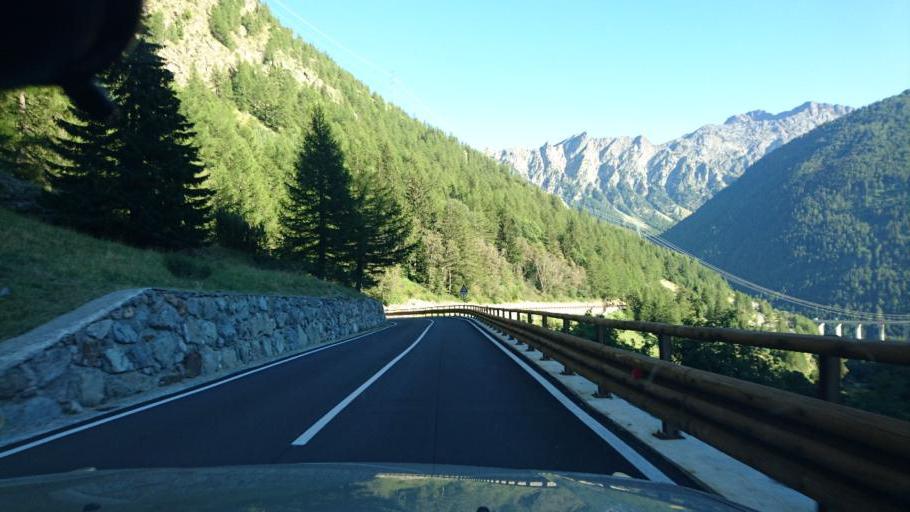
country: IT
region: Aosta Valley
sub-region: Valle d'Aosta
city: San Leonardo
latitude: 45.8328
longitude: 7.1866
